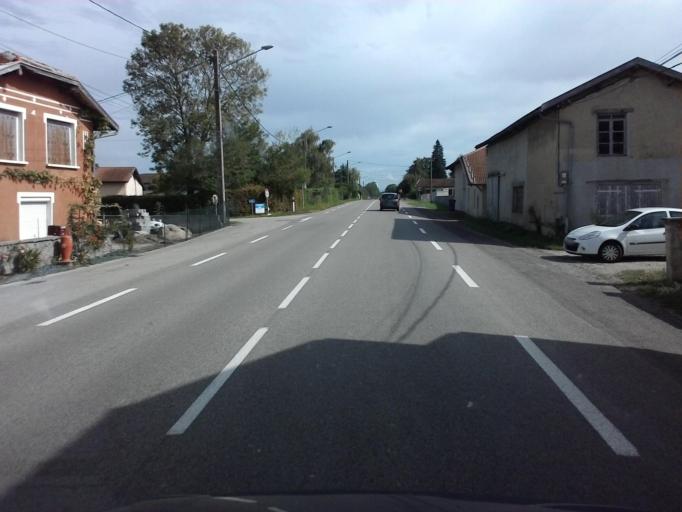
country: FR
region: Rhone-Alpes
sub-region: Departement de l'Ain
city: Polliat
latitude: 46.2484
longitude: 5.1341
